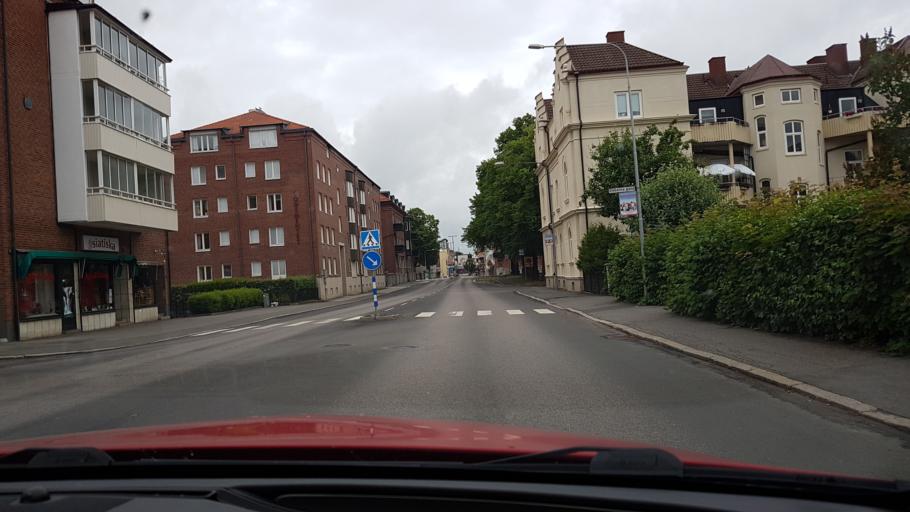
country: SE
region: Vaestra Goetaland
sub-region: Skovde Kommun
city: Skoevde
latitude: 58.3856
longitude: 13.8448
